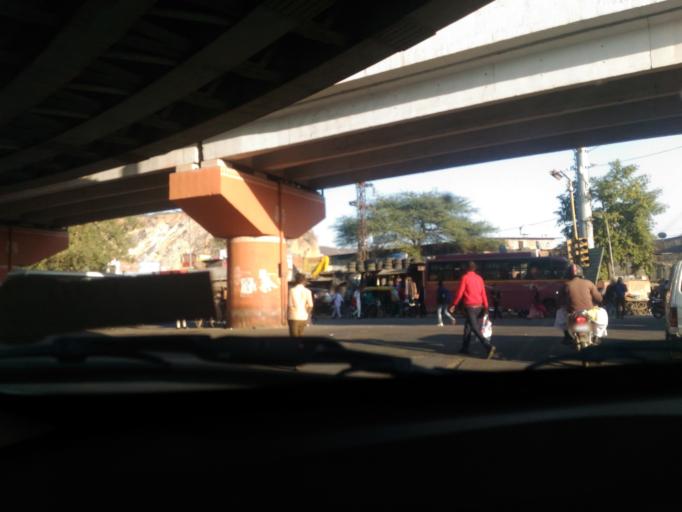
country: IN
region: Rajasthan
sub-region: Jaipur
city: Jaipur
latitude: 26.9045
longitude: 75.8445
